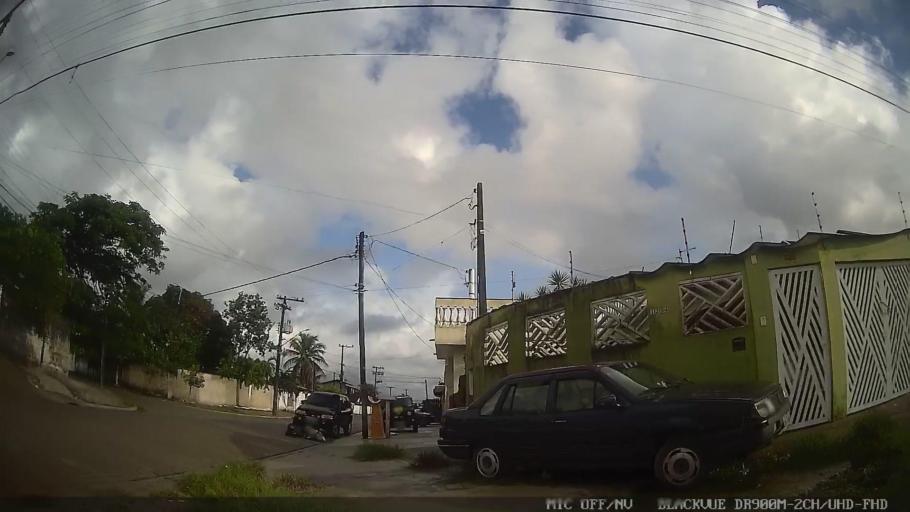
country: BR
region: Sao Paulo
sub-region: Itanhaem
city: Itanhaem
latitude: -24.1806
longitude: -46.8547
